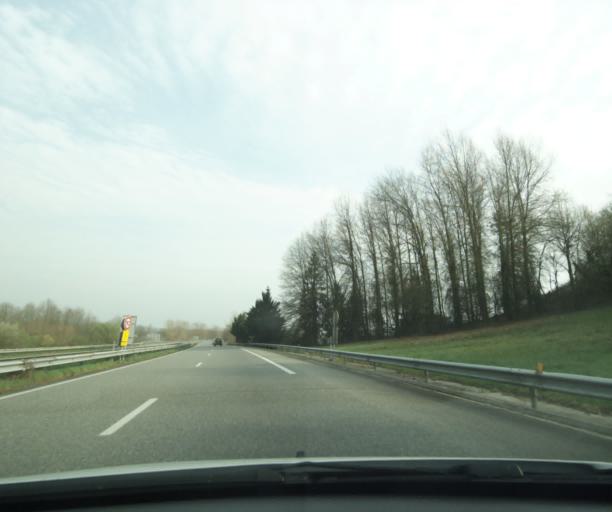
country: FR
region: Aquitaine
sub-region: Departement des Pyrenees-Atlantiques
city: Orthez
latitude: 43.4742
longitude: -0.7622
